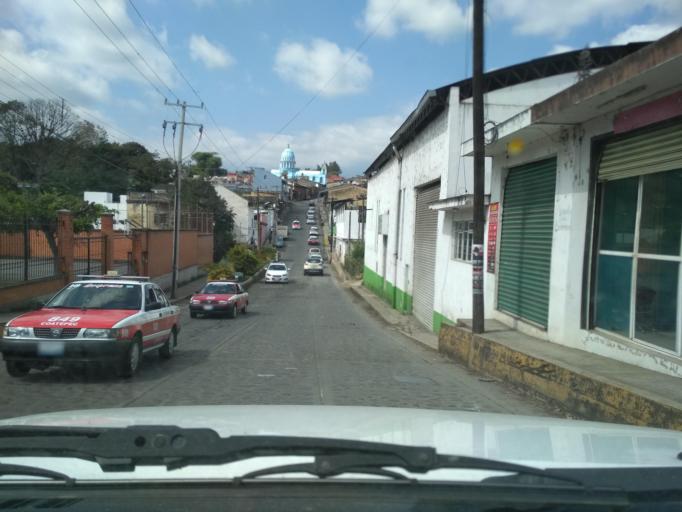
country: MX
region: Veracruz
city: Coatepec
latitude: 19.4516
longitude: -96.9510
